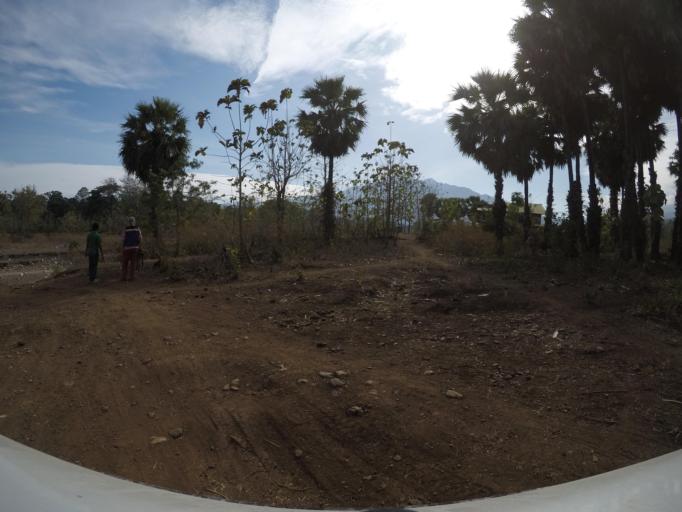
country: TL
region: Bobonaro
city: Maliana
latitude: -8.9932
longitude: 125.2051
